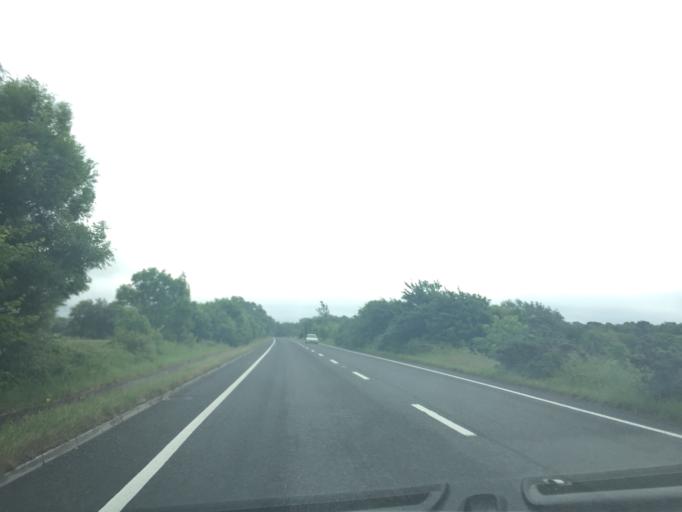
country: GB
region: England
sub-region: Dorset
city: Wareham
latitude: 50.6780
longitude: -2.1199
